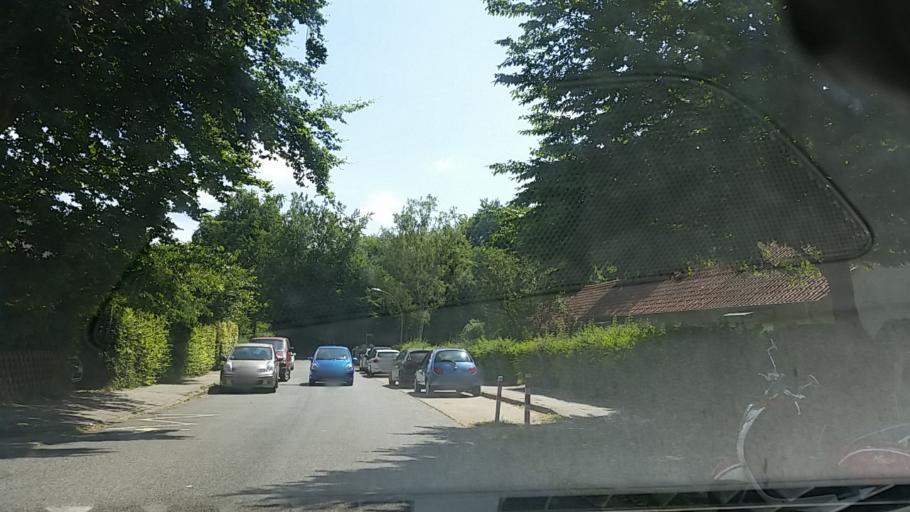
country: DE
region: Schleswig-Holstein
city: Halstenbek
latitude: 53.5810
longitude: 9.8096
